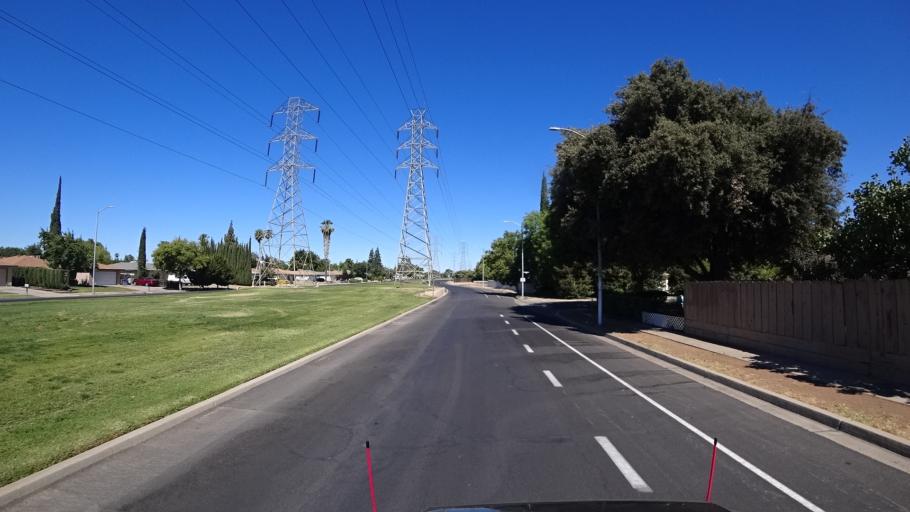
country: US
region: California
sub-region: Fresno County
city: Fresno
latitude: 36.7987
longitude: -119.8361
